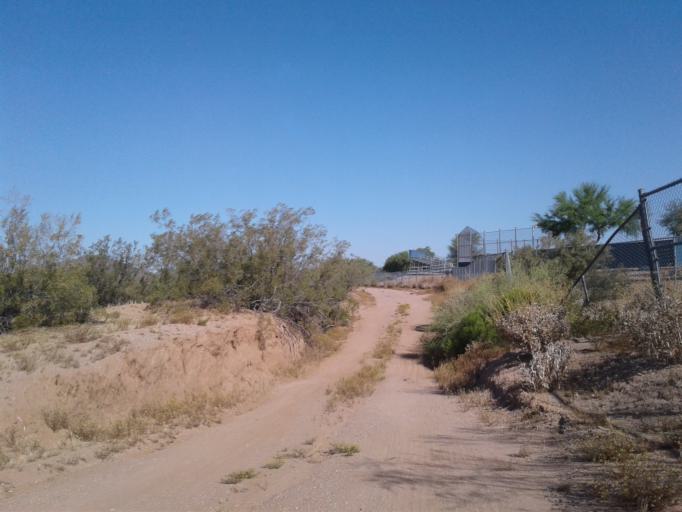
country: US
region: Arizona
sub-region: Maricopa County
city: Paradise Valley
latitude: 33.6775
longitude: -112.0079
